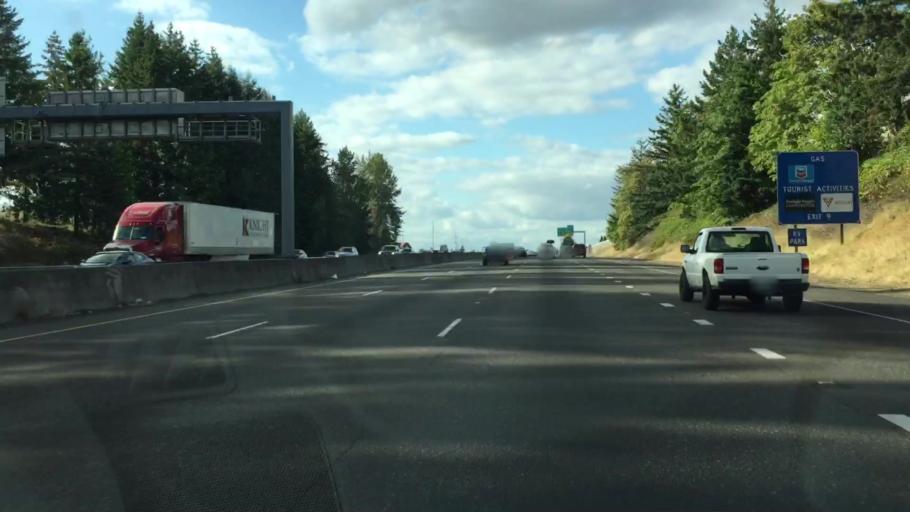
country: US
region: Washington
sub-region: Clark County
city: Mount Vista
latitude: 45.7401
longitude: -122.6585
